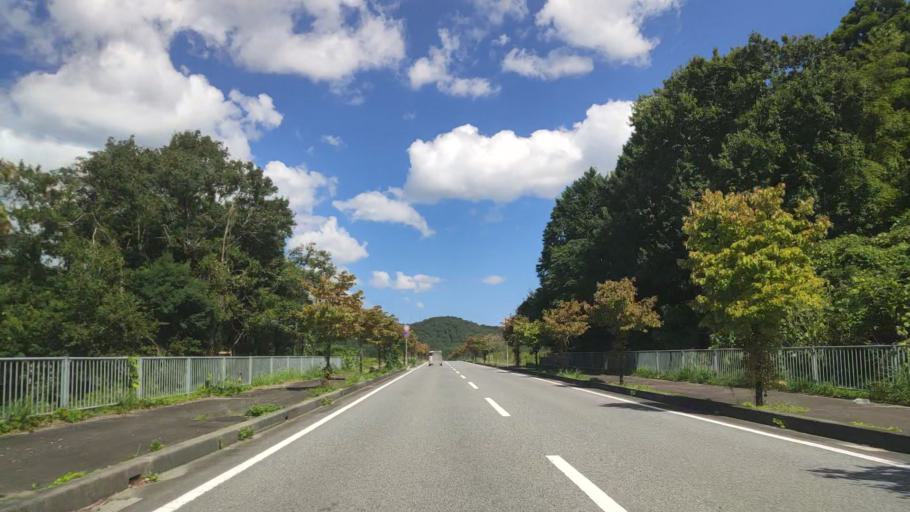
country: JP
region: Kyoto
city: Fukuchiyama
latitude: 35.2524
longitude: 135.1403
